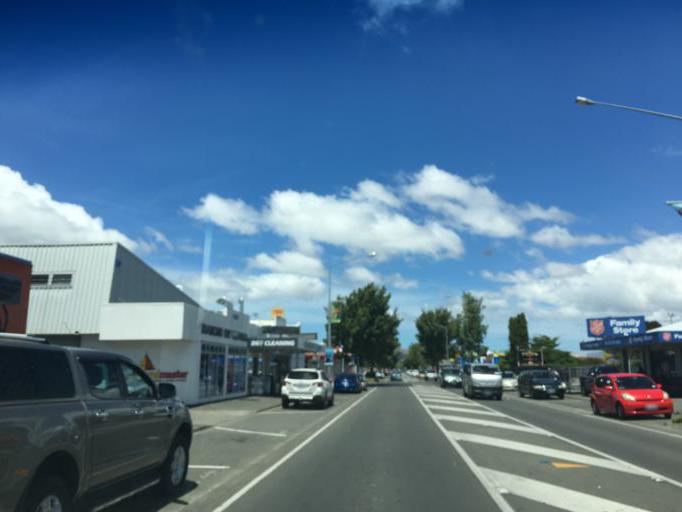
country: NZ
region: Hawke's Bay
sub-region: Hastings District
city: Hastings
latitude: -39.6346
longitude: 176.8355
